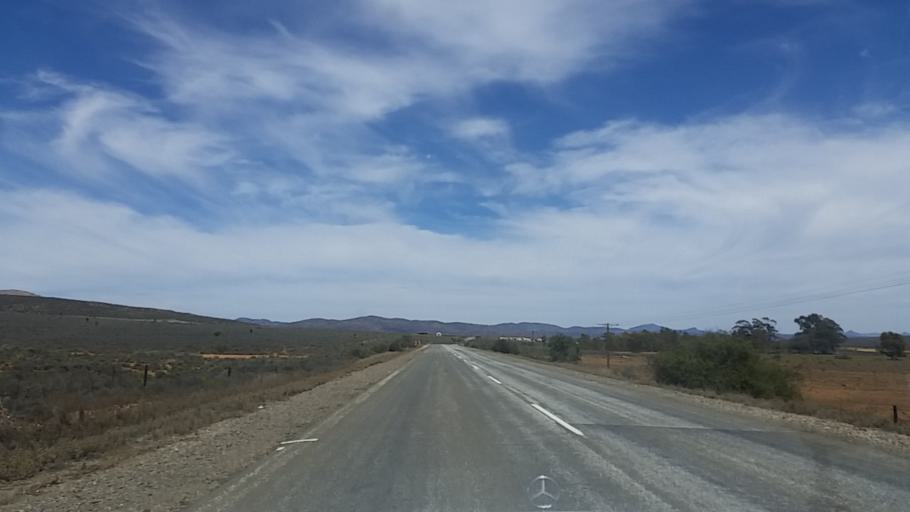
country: ZA
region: Western Cape
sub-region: Eden District Municipality
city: Knysna
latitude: -33.5985
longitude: 23.1500
